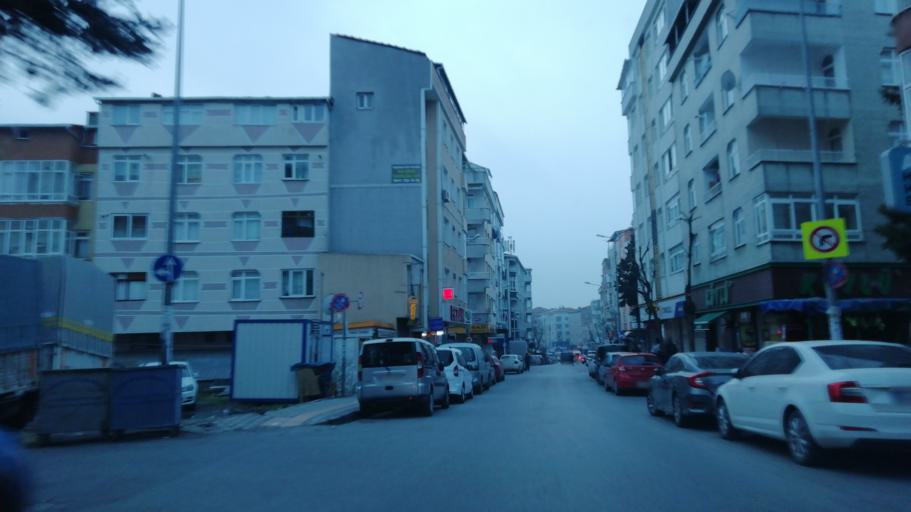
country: TR
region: Istanbul
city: Bahcelievler
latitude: 41.0038
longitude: 28.8309
